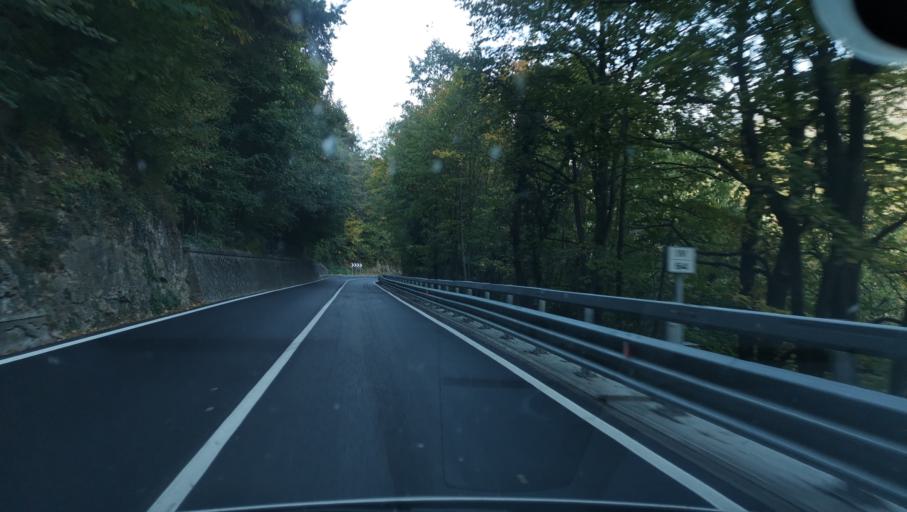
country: IT
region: Piedmont
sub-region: Provincia di Torino
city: Chiomonte
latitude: 45.1107
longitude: 6.9643
